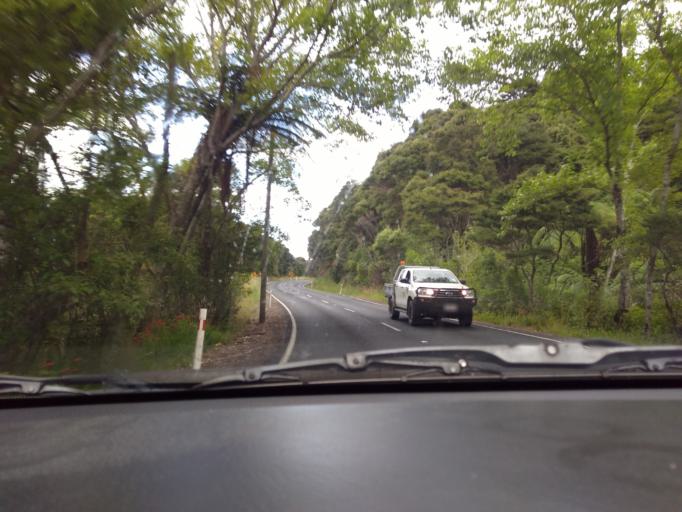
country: NZ
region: Auckland
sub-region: Auckland
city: Titirangi
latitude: -37.0056
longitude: 174.5823
